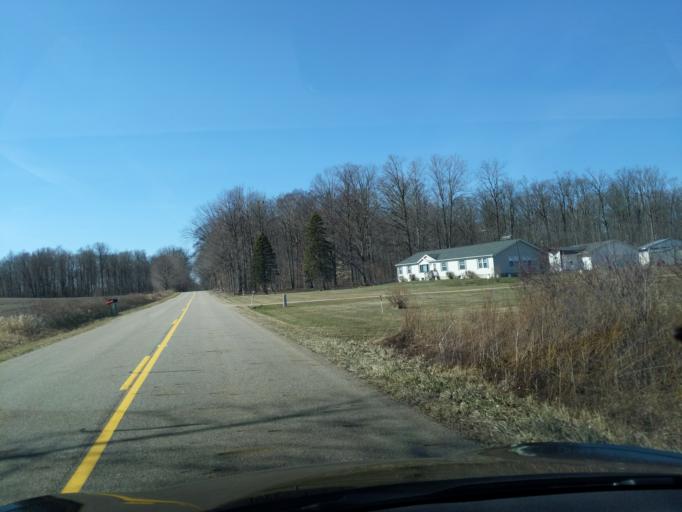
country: US
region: Michigan
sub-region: Ionia County
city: Lake Odessa
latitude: 42.7270
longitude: -85.0389
